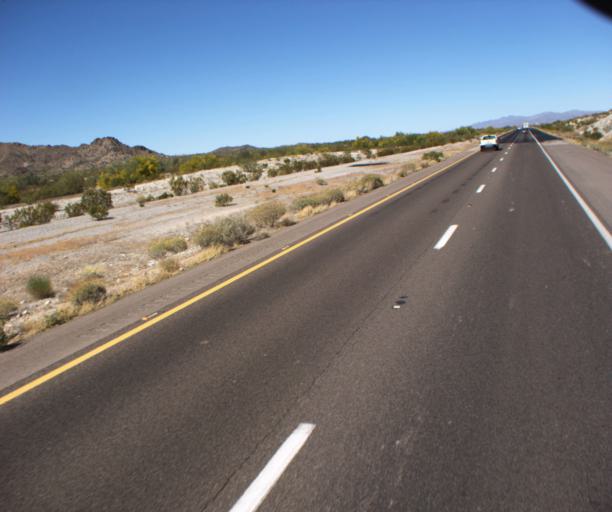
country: US
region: Arizona
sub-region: Maricopa County
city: Buckeye
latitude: 33.2482
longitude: -112.6373
